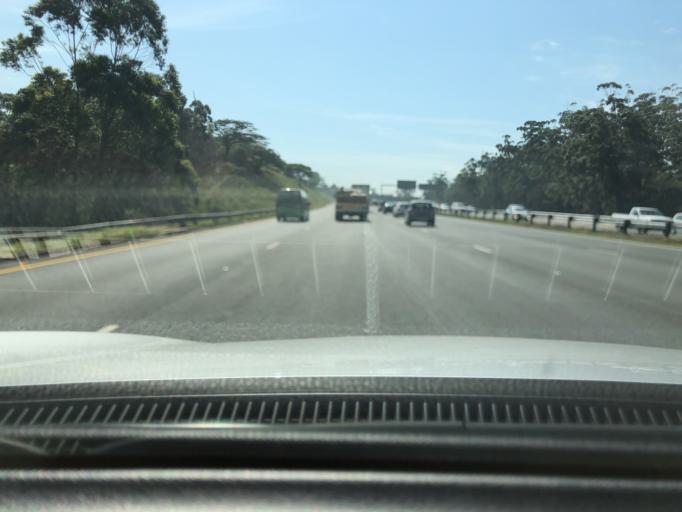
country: ZA
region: KwaZulu-Natal
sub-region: eThekwini Metropolitan Municipality
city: Berea
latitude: -29.8351
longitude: 30.9592
